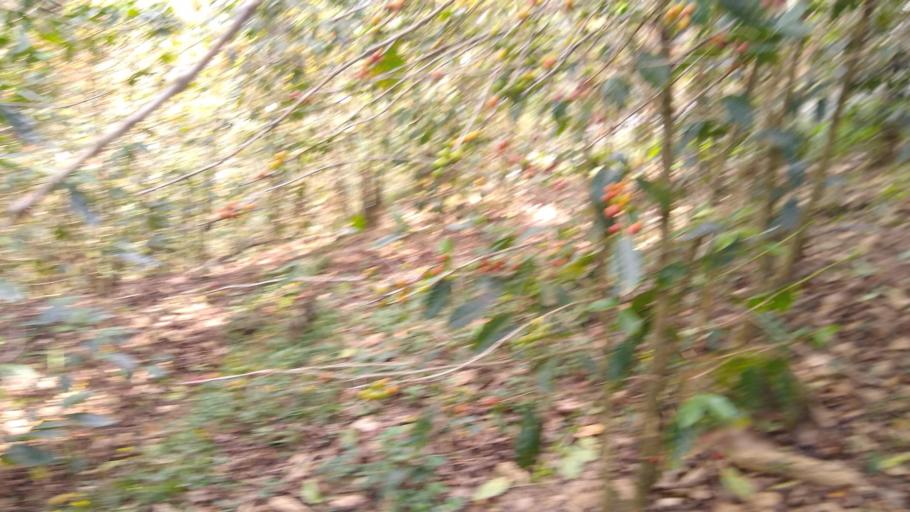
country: MX
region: Puebla
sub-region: Tepetzintla
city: Tlamanca de Hernandez
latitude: 19.9333
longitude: -97.8149
